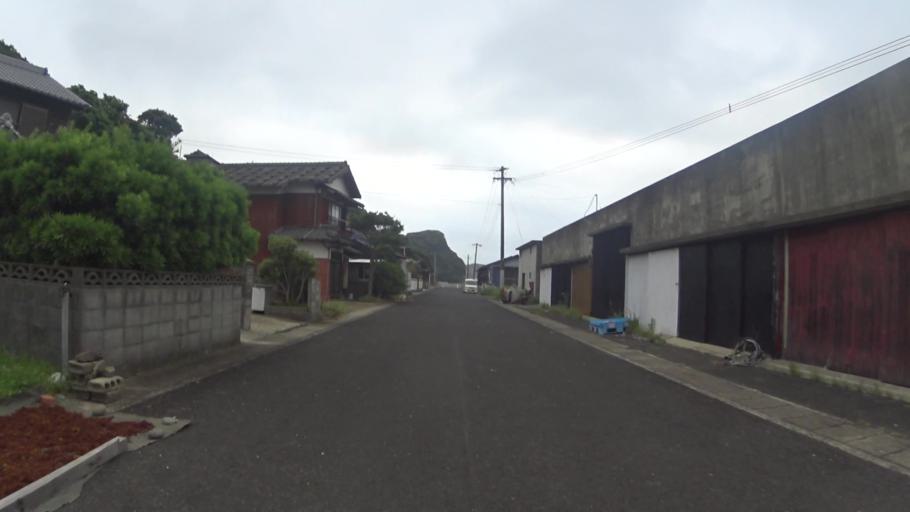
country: JP
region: Nagasaki
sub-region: Hirado Shi
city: Hirado
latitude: 33.1915
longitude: 129.3588
